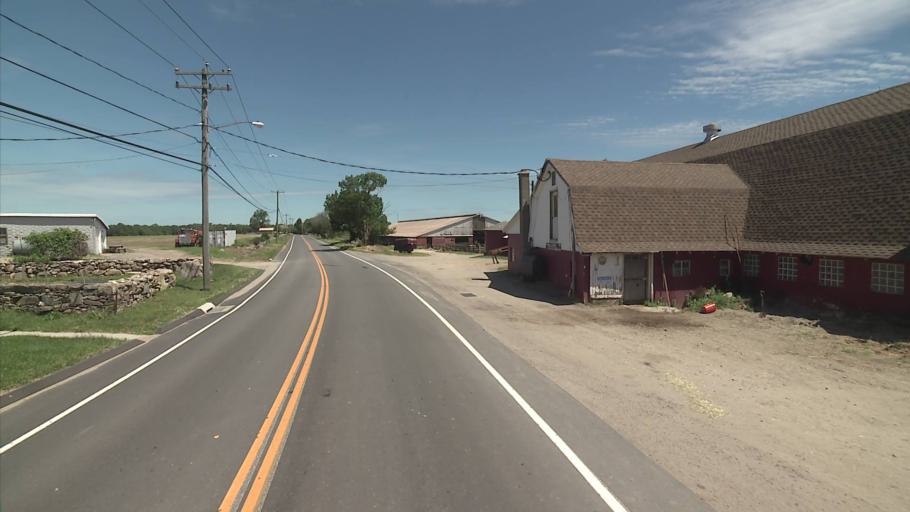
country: US
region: Connecticut
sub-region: Windham County
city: Moosup
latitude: 41.6494
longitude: -71.8470
